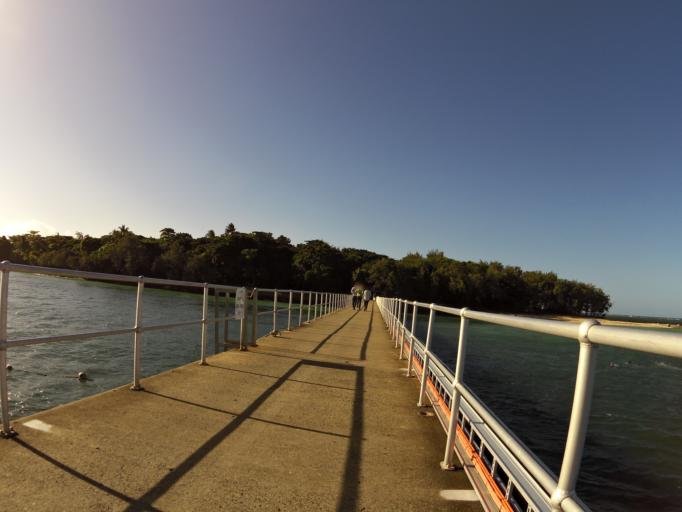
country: AU
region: Queensland
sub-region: Cairns
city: Yorkeys Knob
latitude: -16.7582
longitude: 145.9704
